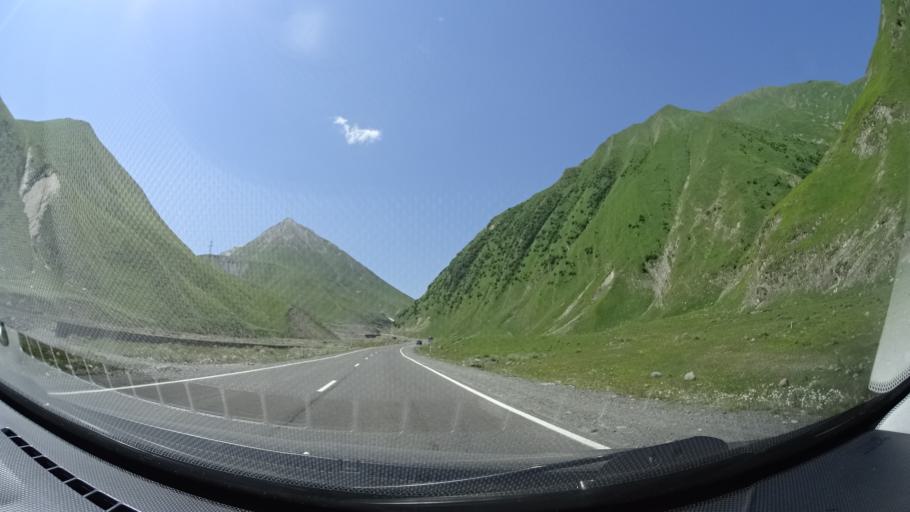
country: GE
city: Gudauri
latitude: 42.5517
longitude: 44.4957
